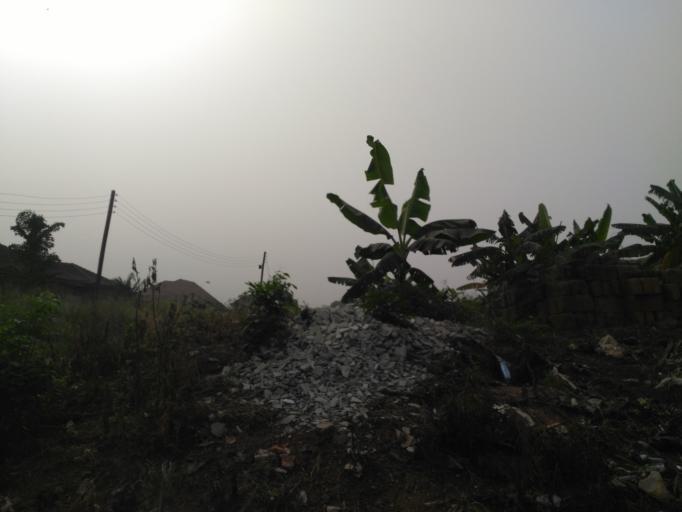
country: GH
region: Ashanti
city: Kumasi
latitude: 6.6538
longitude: -1.6276
